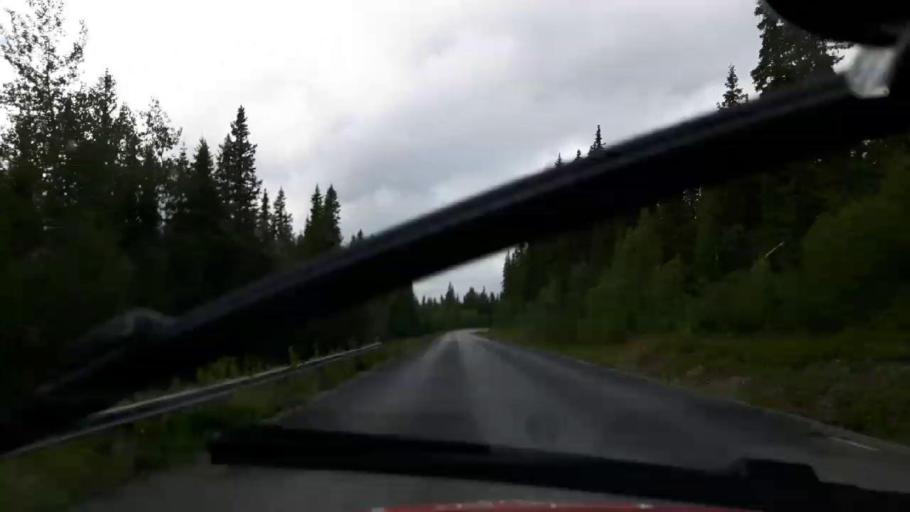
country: SE
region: Vaesterbotten
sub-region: Vilhelmina Kommun
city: Sjoberg
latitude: 64.9359
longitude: 15.7245
